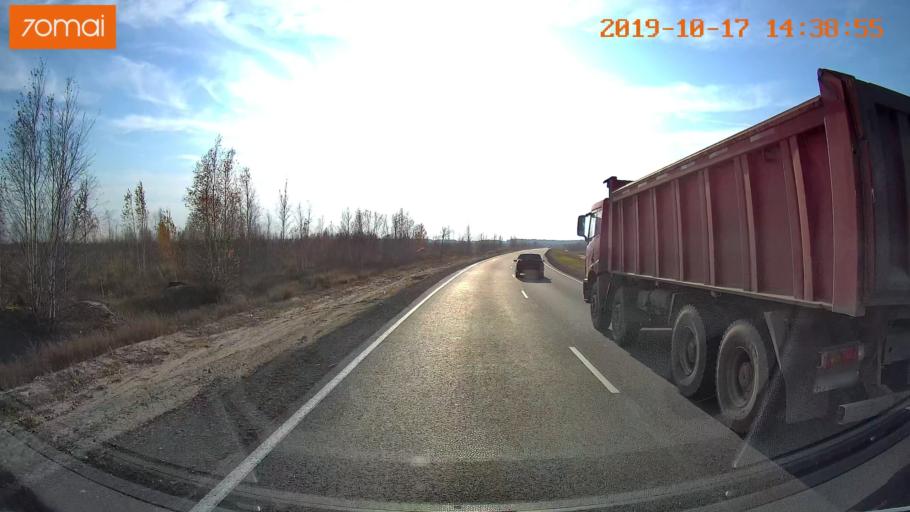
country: RU
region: Rjazan
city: Solotcha
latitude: 54.8663
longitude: 39.9804
